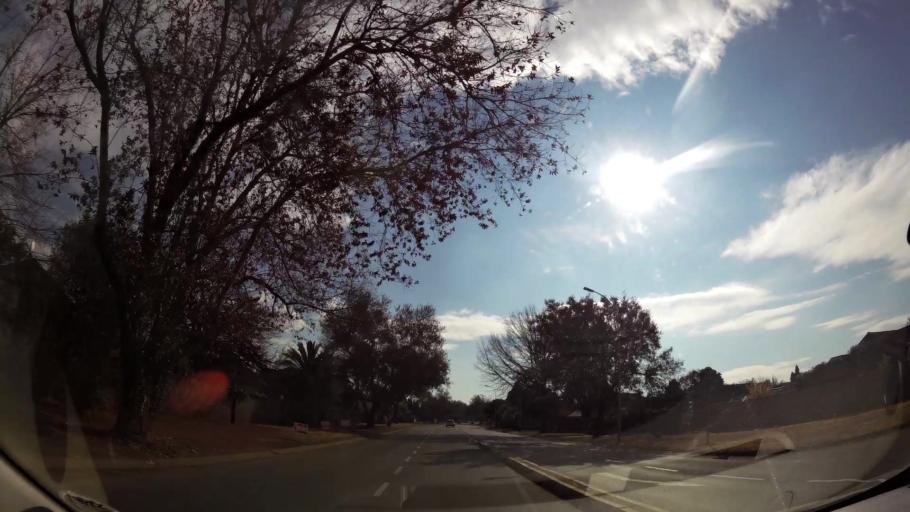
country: ZA
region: Gauteng
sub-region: Sedibeng District Municipality
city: Meyerton
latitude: -26.5545
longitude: 28.0320
